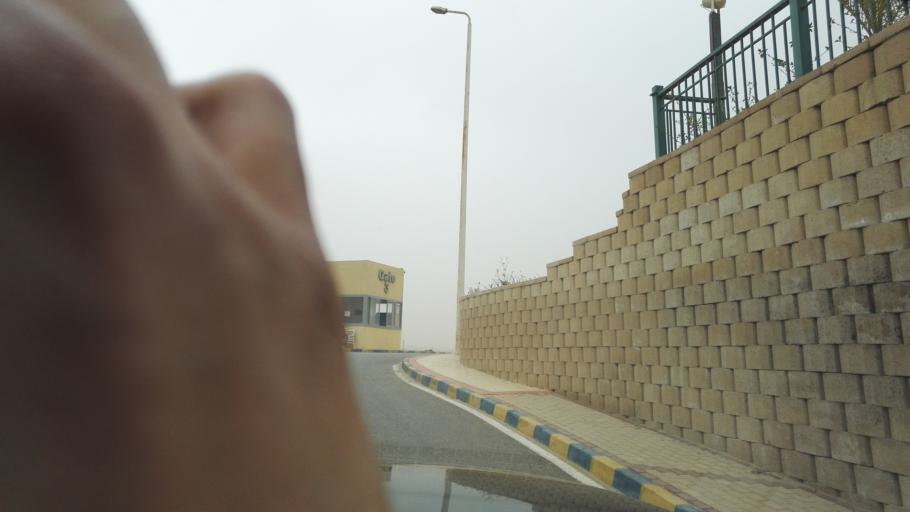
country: EG
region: Muhafazat al Qalyubiyah
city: Al Khankah
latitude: 30.0376
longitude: 31.5287
